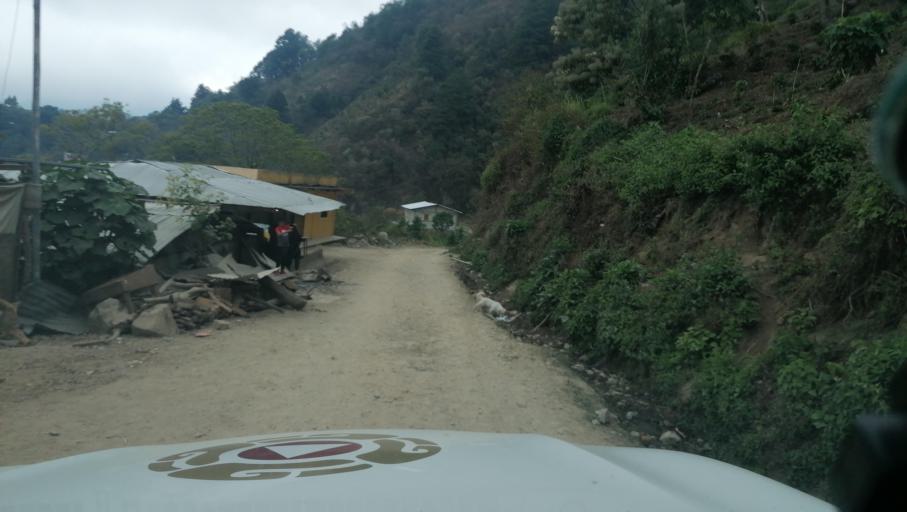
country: GT
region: San Marcos
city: Tacana
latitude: 15.2061
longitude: -92.1752
